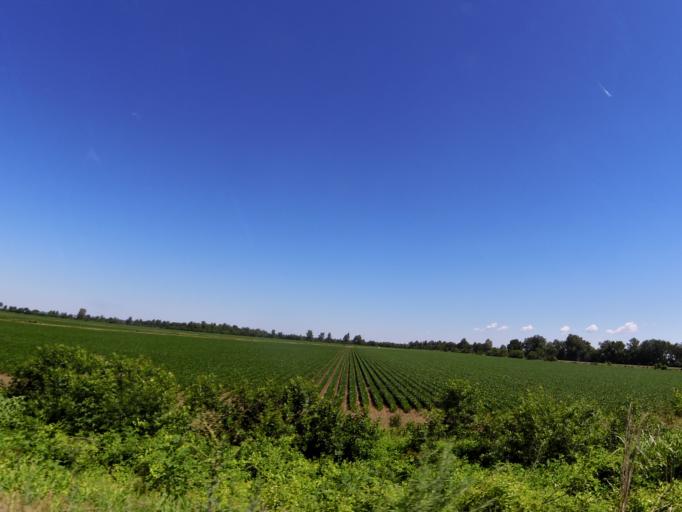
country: US
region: Missouri
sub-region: New Madrid County
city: Lilbourn
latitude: 36.5552
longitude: -89.6157
